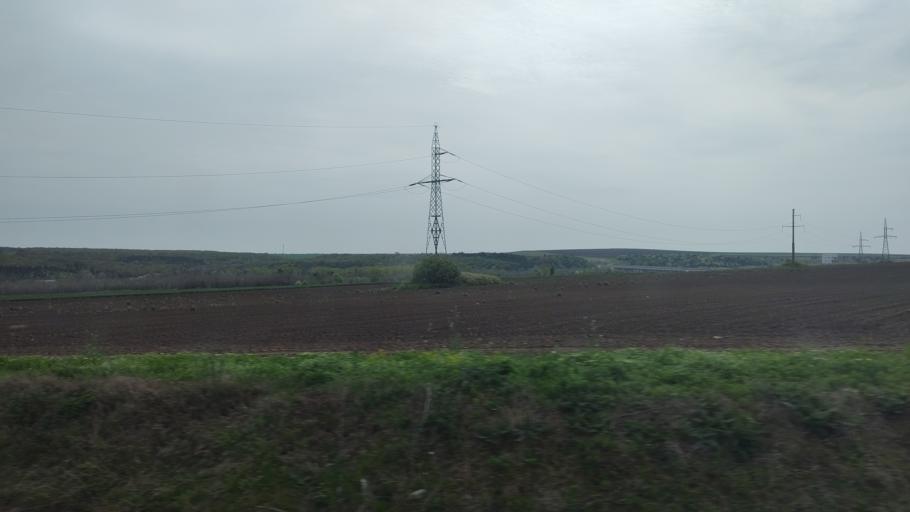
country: RO
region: Constanta
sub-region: Oras Murfatlar
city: Siminoc
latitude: 44.1472
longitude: 28.3659
